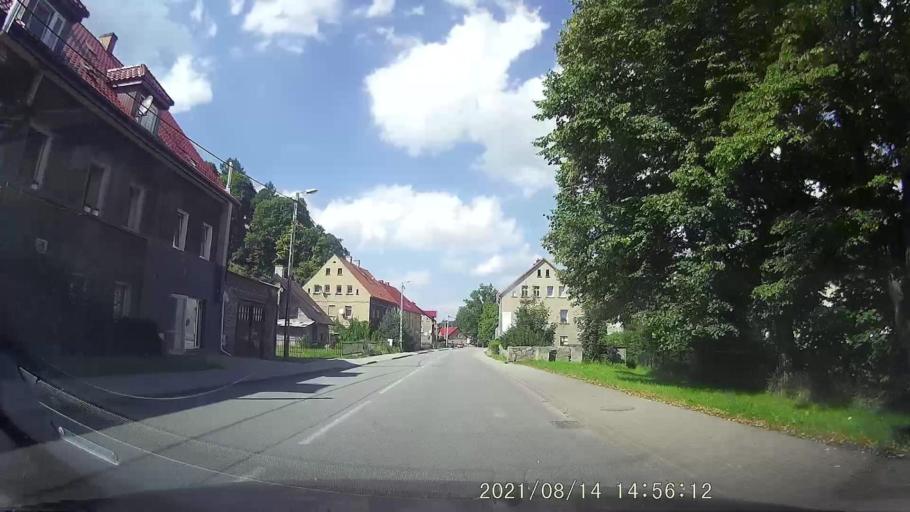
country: PL
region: Lower Silesian Voivodeship
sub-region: Powiat walbrzyski
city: Gluszyca
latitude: 50.6881
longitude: 16.3710
